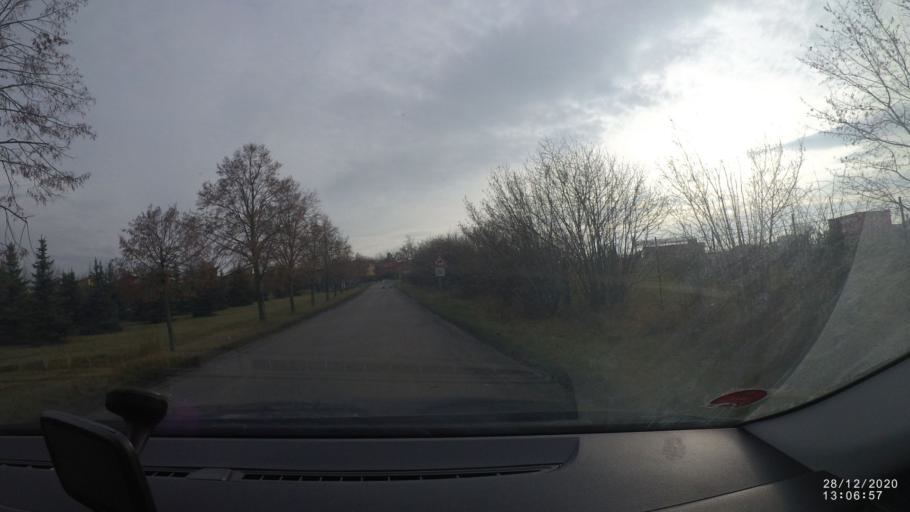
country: CZ
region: Central Bohemia
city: Zelenec
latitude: 50.1392
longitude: 14.6586
